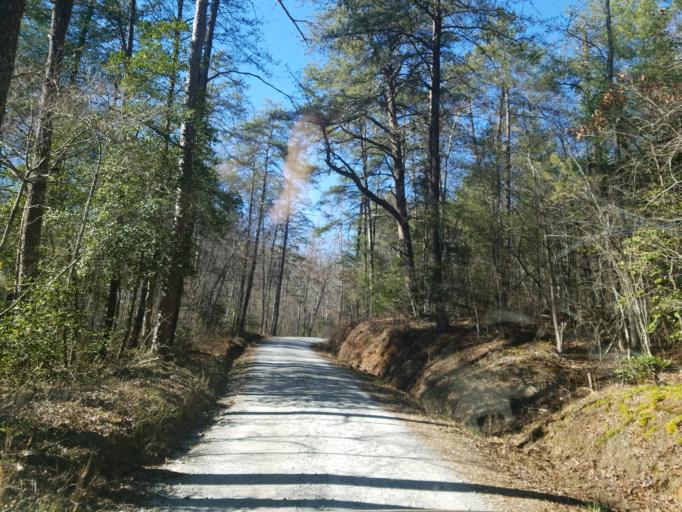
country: US
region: Georgia
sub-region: Dawson County
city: Dawsonville
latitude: 34.5083
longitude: -84.2543
